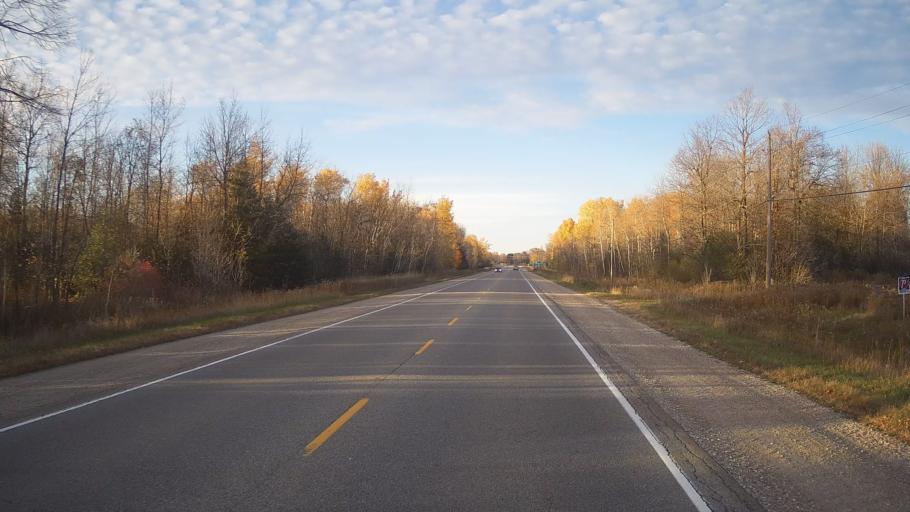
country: CA
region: Ontario
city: Perth
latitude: 45.0068
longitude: -76.2299
